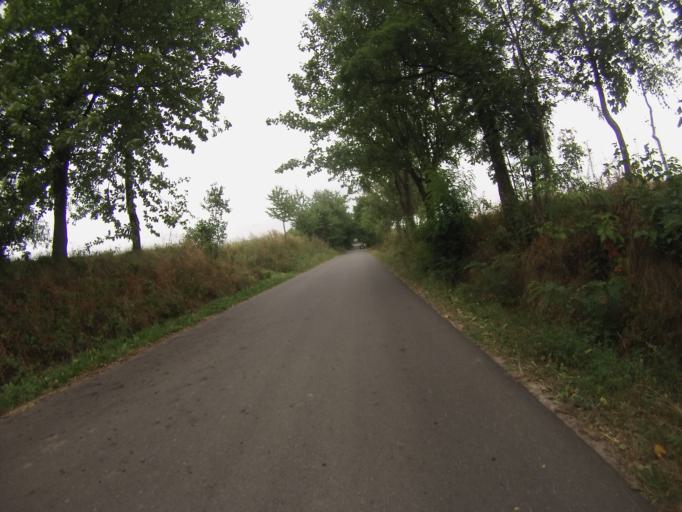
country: PL
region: Swietokrzyskie
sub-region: Powiat kielecki
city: Lagow
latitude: 50.7397
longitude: 21.0506
